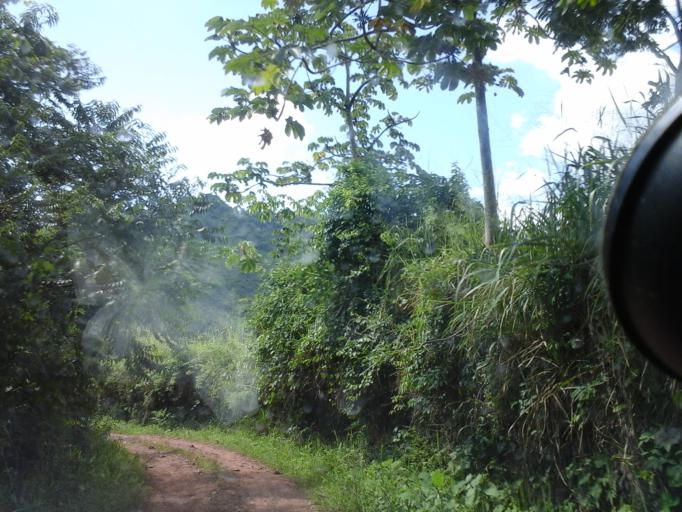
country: CO
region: Cesar
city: San Diego
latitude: 10.2728
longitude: -73.0931
